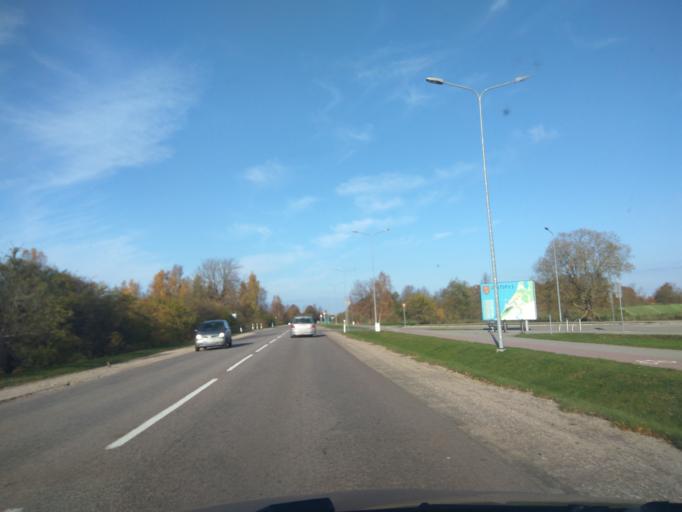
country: LV
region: Ventspils
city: Ventspils
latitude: 57.3588
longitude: 21.5634
